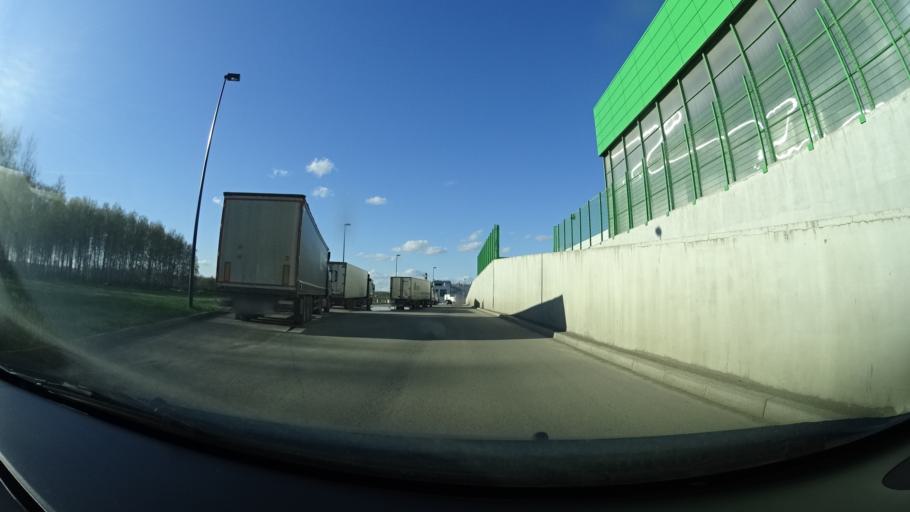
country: RU
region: Bashkortostan
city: Ufa
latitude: 54.6704
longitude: 55.9270
